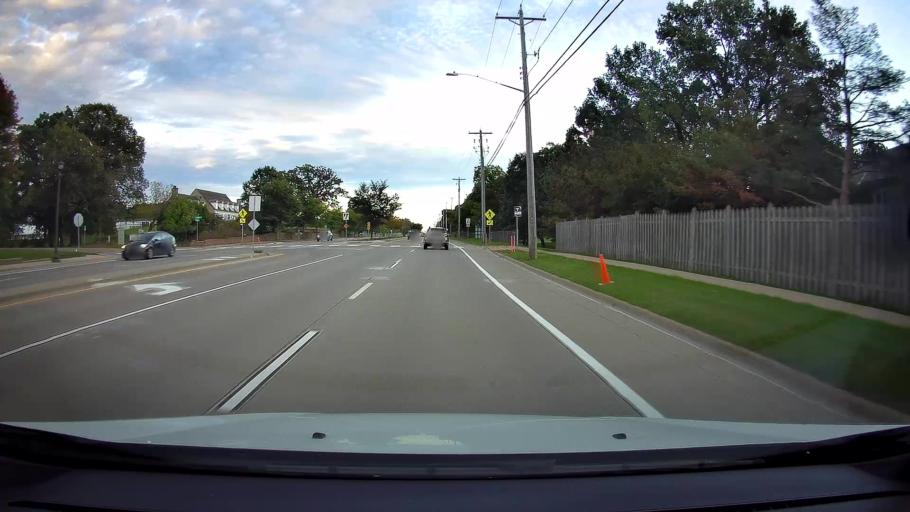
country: US
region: Minnesota
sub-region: Ramsey County
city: Lauderdale
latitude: 44.9916
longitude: -93.1979
